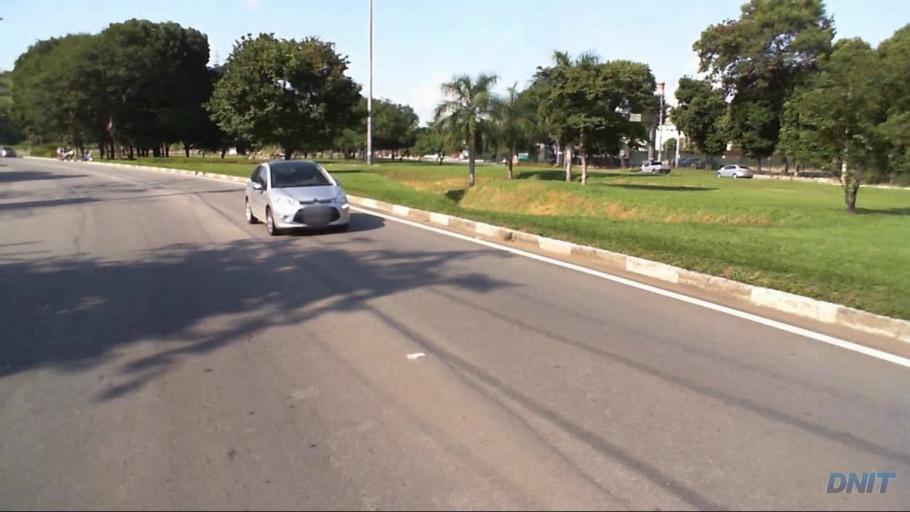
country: BR
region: Minas Gerais
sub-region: Ipatinga
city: Ipatinga
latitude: -19.4858
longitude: -42.5560
